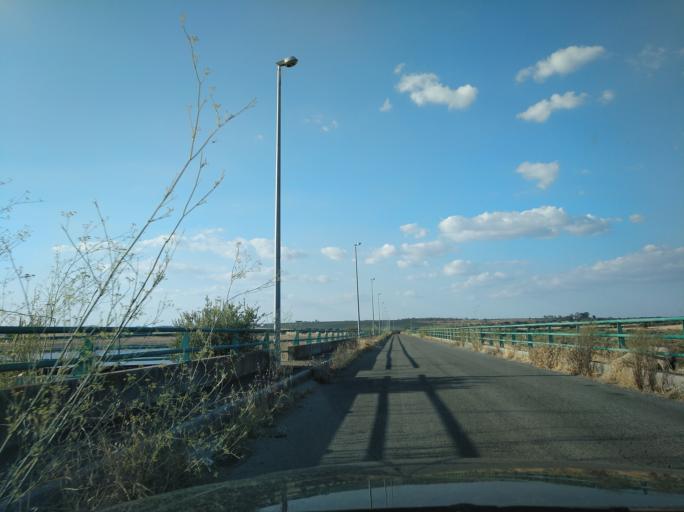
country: PT
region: Portalegre
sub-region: Campo Maior
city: Campo Maior
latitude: 39.0950
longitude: -7.1216
